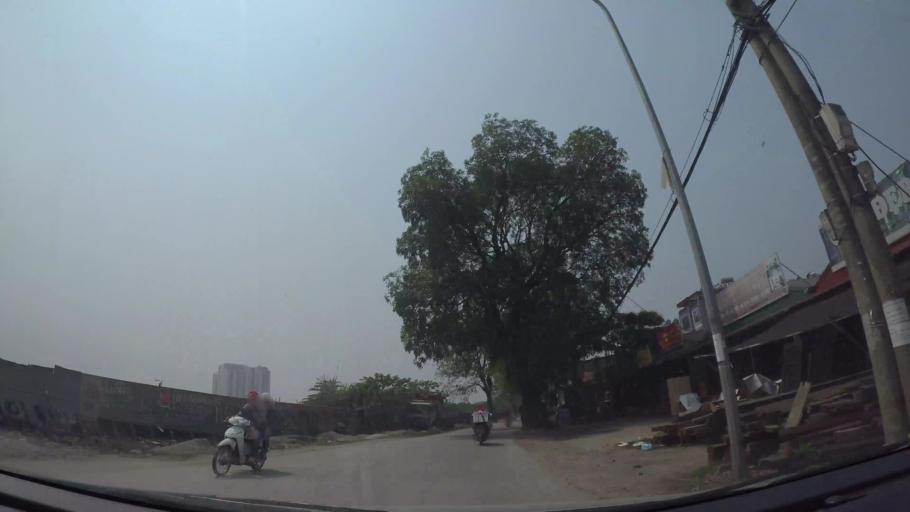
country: VN
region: Ha Noi
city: Ha Dong
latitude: 20.9895
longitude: 105.7646
